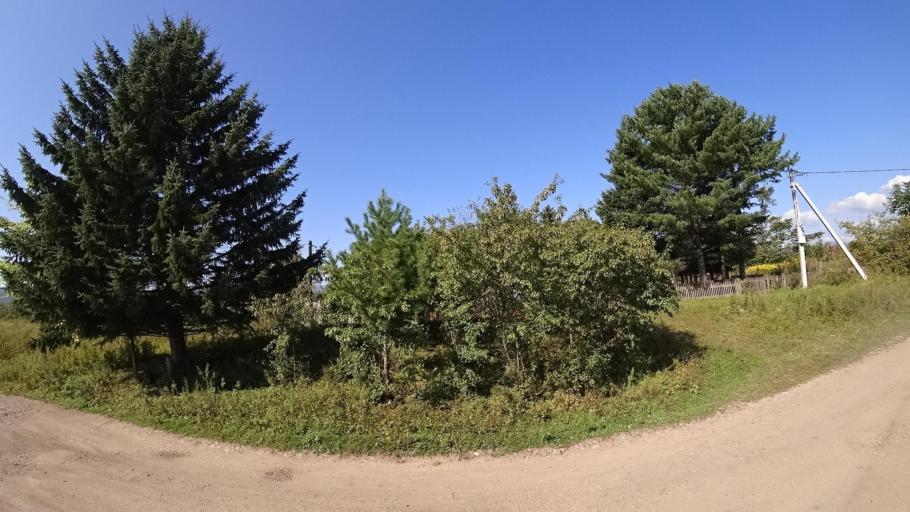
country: RU
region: Jewish Autonomous Oblast
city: Bira
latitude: 48.9948
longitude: 132.4540
